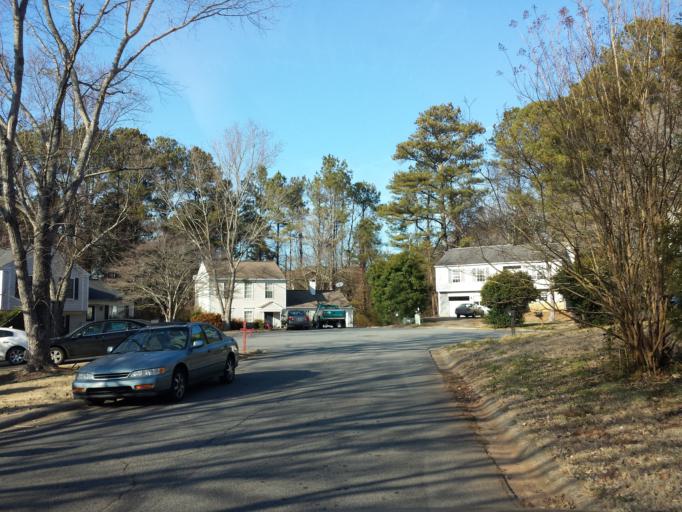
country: US
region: Georgia
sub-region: Cherokee County
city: Woodstock
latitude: 34.0582
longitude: -84.5227
